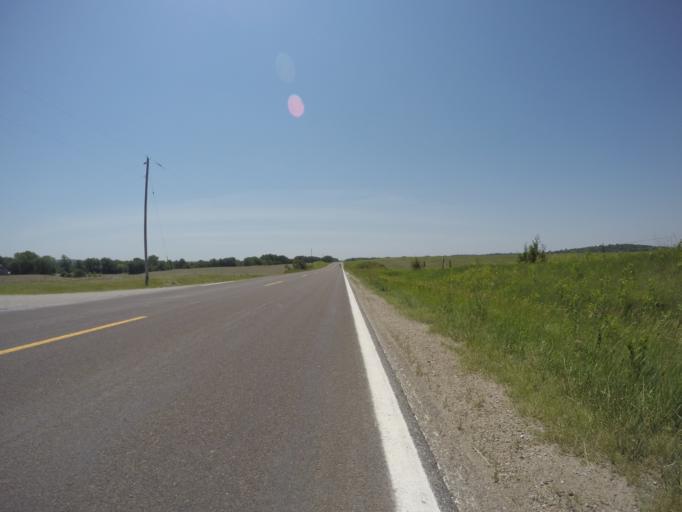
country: US
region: Nebraska
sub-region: Pawnee County
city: Pawnee City
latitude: 40.0139
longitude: -96.0484
